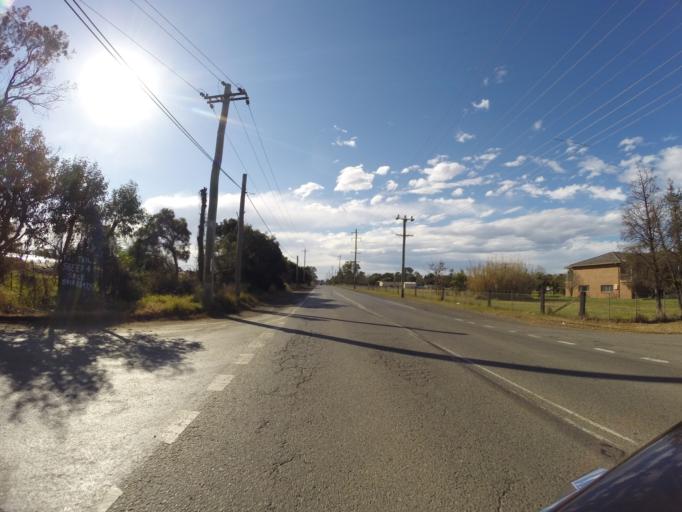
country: AU
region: New South Wales
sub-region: Fairfield
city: Cecil Park
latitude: -33.8910
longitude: 150.7907
